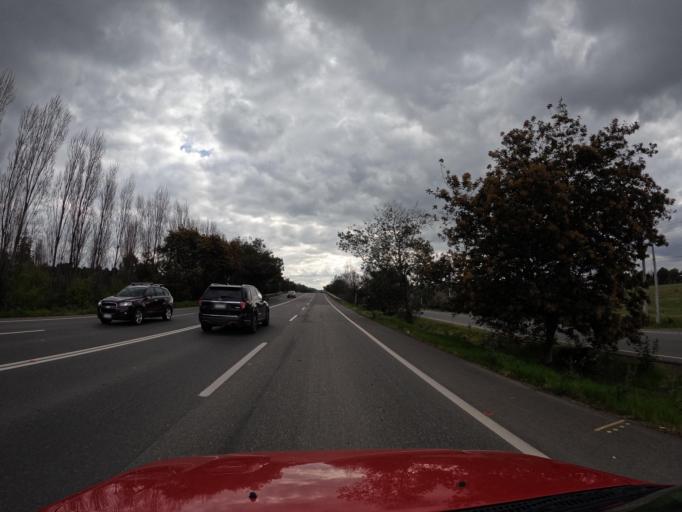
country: CL
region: Maule
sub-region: Provincia de Linares
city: San Javier
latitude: -35.6257
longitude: -71.7464
